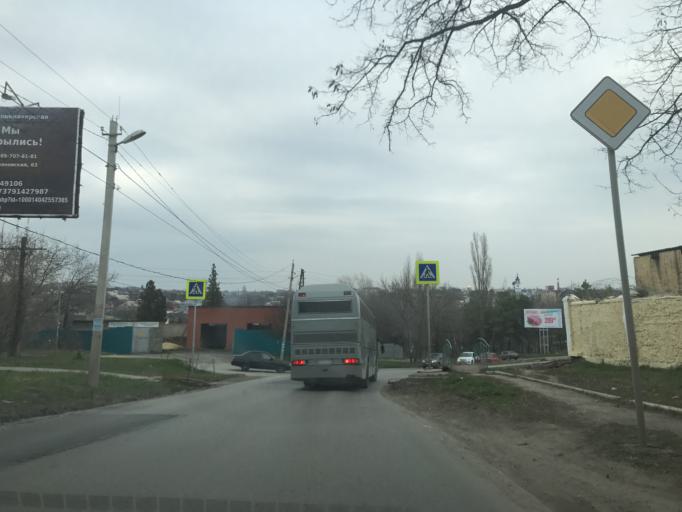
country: RU
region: Rostov
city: Novocherkassk
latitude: 47.4027
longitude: 40.0768
